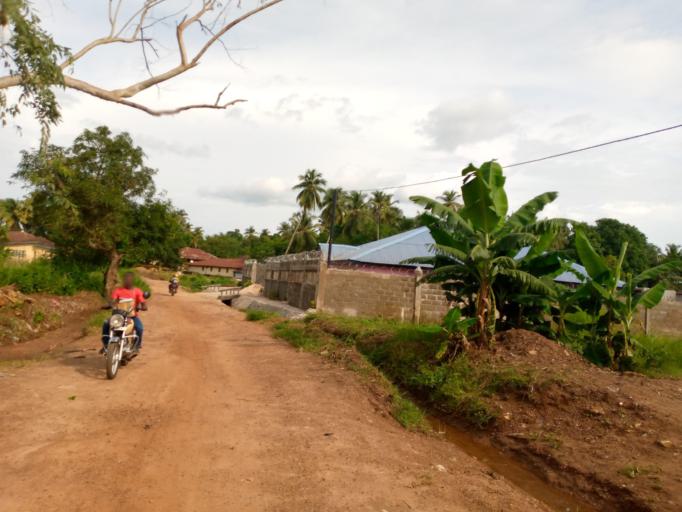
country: SL
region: Northern Province
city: Magburaka
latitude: 8.7201
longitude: -11.9518
